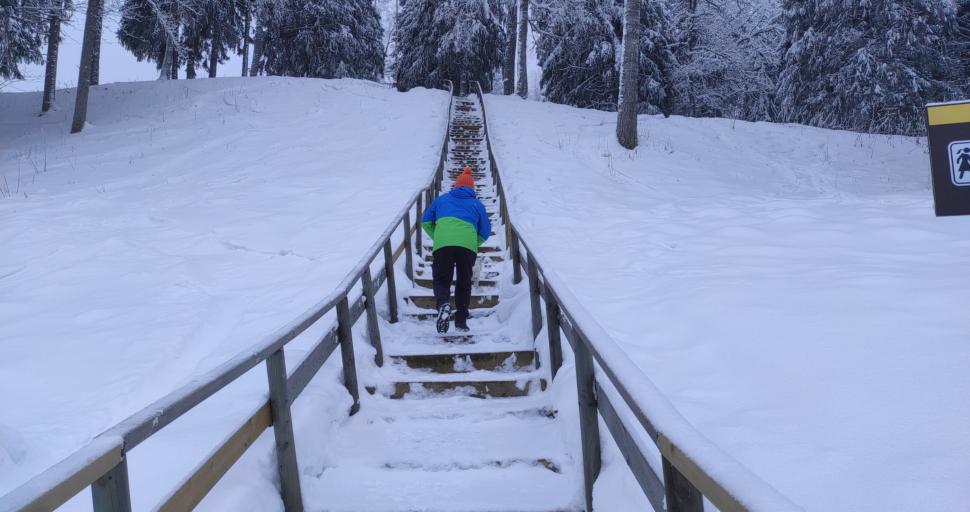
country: LV
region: Vecpiebalga
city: Vecpiebalga
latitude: 56.8755
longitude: 25.9625
